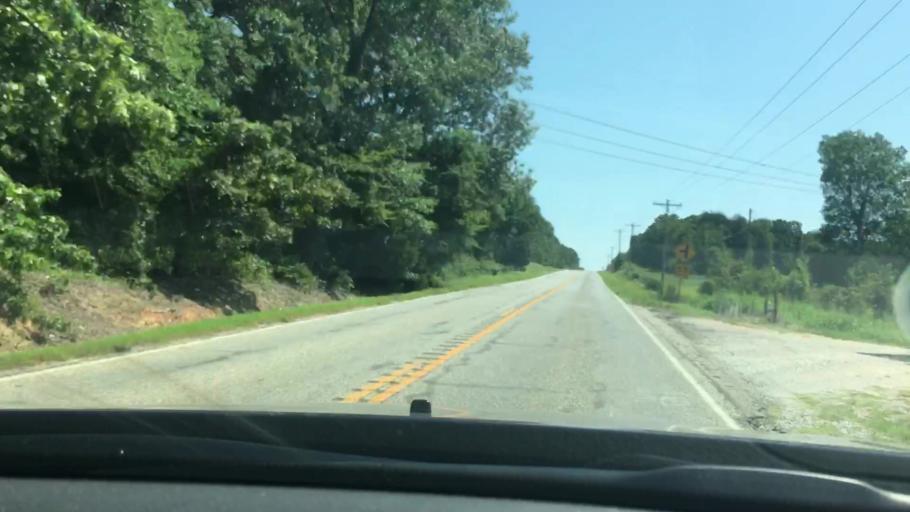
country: US
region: Oklahoma
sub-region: Johnston County
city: Tishomingo
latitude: 34.2377
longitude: -96.5892
